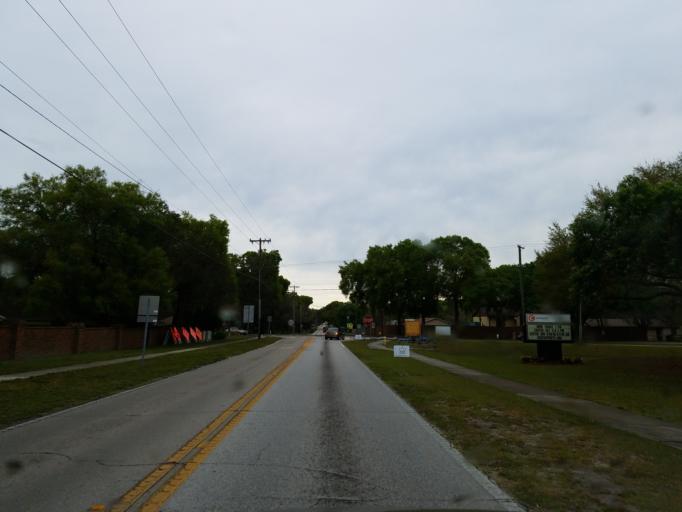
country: US
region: Florida
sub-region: Hillsborough County
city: Bloomingdale
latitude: 27.9107
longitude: -82.2442
